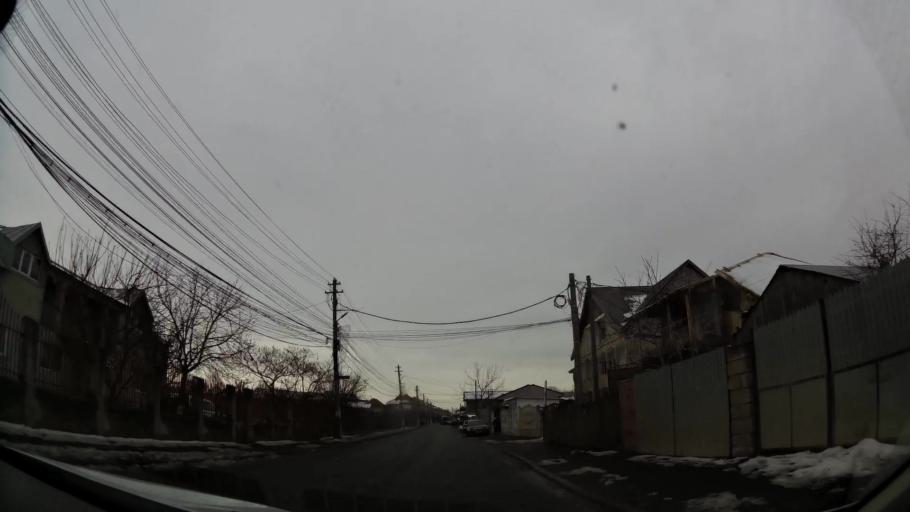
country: RO
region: Ilfov
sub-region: Comuna Pantelimon
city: Pantelimon
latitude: 44.4577
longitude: 26.2092
